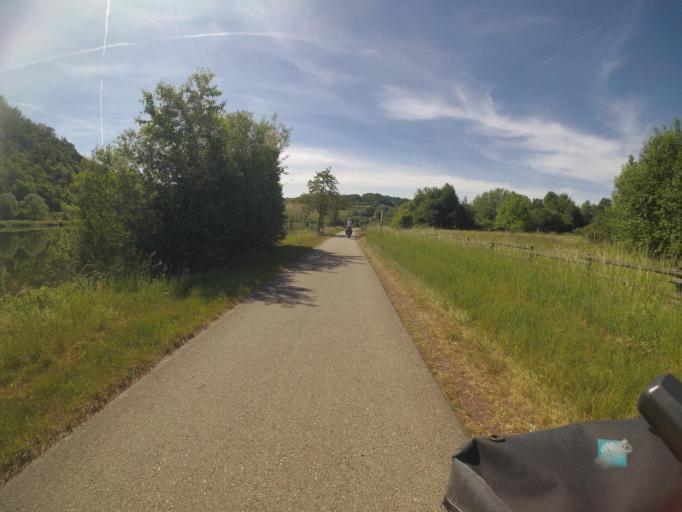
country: DE
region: Rheinland-Pfalz
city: Schoden
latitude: 49.6289
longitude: 6.5747
